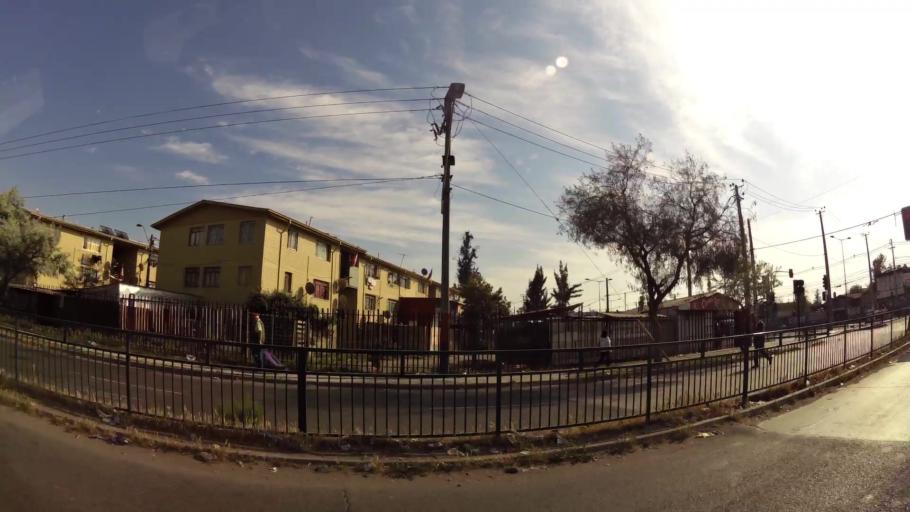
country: CL
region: Santiago Metropolitan
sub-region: Provincia de Santiago
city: La Pintana
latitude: -33.5540
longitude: -70.6323
